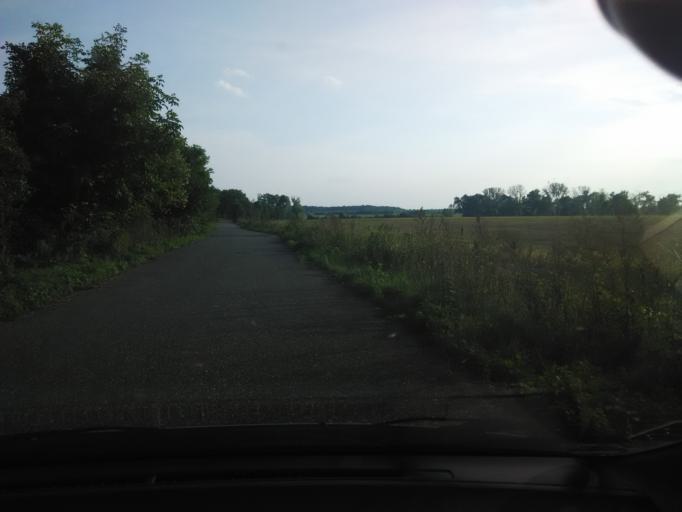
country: SK
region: Banskobystricky
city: Nova Bana
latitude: 48.3106
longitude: 18.7011
